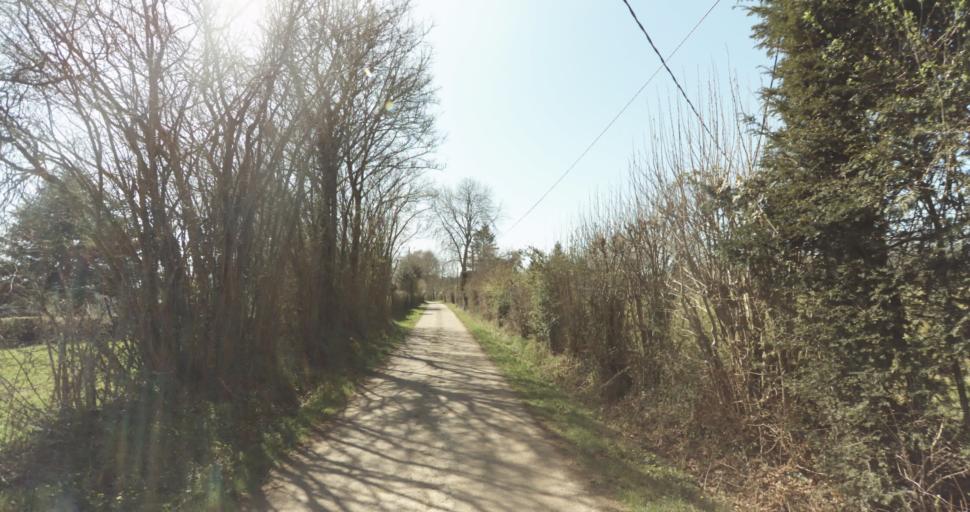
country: FR
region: Lower Normandy
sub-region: Departement du Calvados
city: Saint-Pierre-sur-Dives
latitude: 48.9949
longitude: 0.0573
